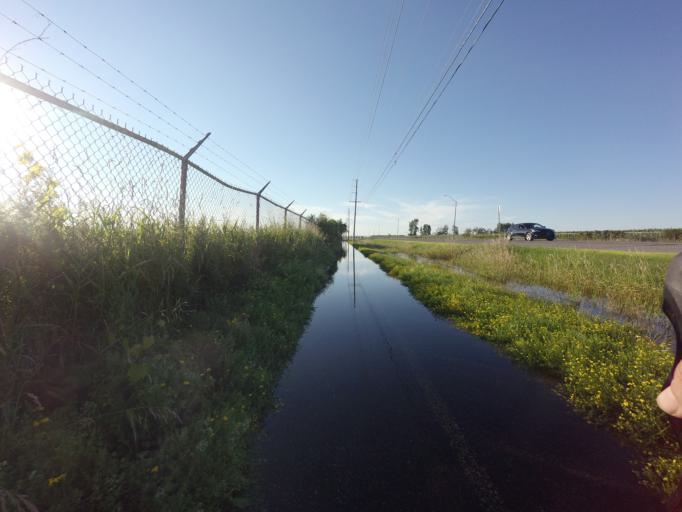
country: CA
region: Ontario
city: Bells Corners
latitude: 45.2985
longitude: -75.7634
